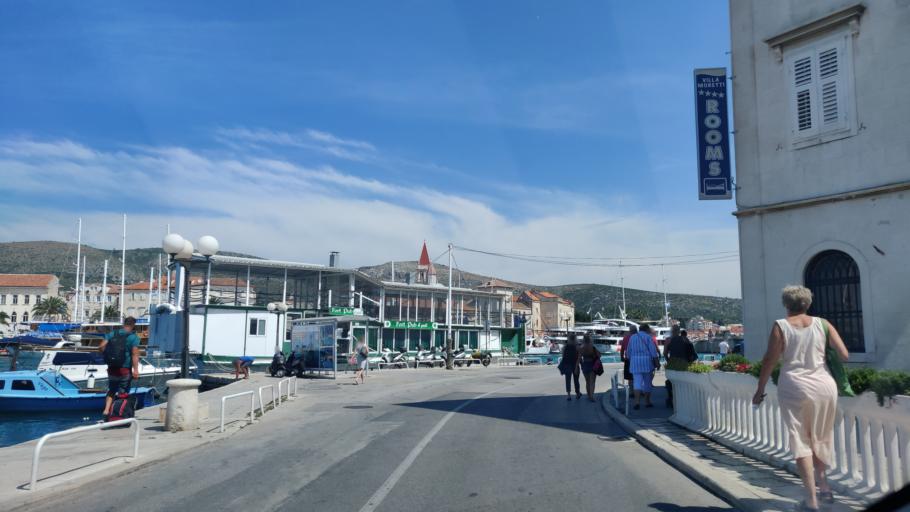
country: HR
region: Splitsko-Dalmatinska
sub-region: Grad Trogir
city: Trogir
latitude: 43.5142
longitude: 16.2506
